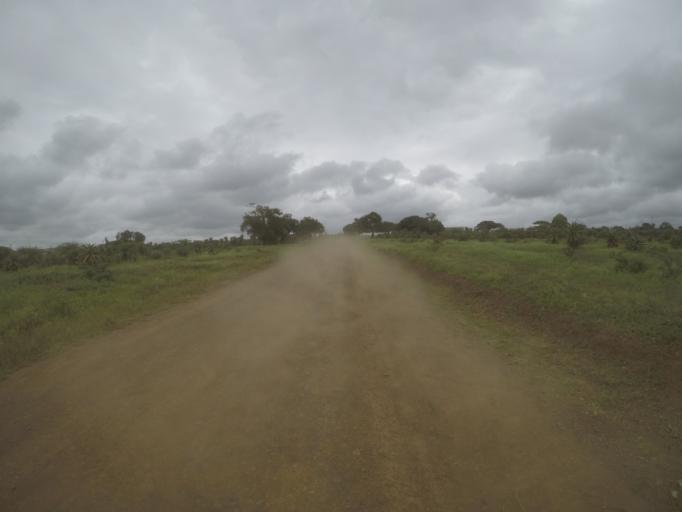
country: ZA
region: KwaZulu-Natal
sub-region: uThungulu District Municipality
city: Empangeni
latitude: -28.6047
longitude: 31.8703
